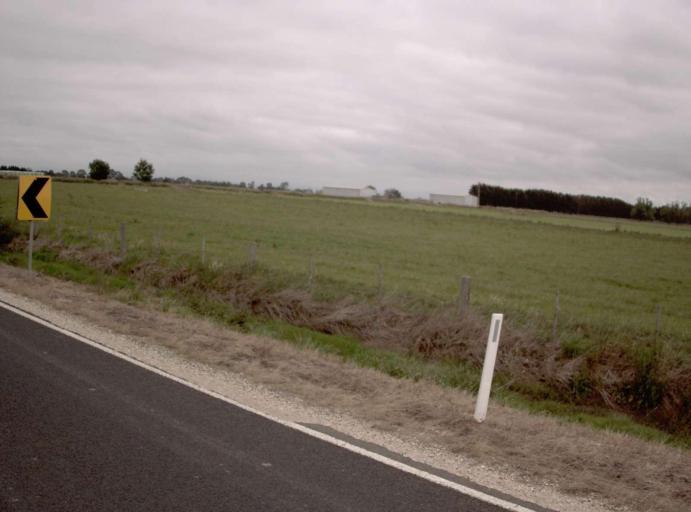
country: AU
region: Victoria
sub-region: Wellington
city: Sale
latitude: -38.0569
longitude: 146.9663
